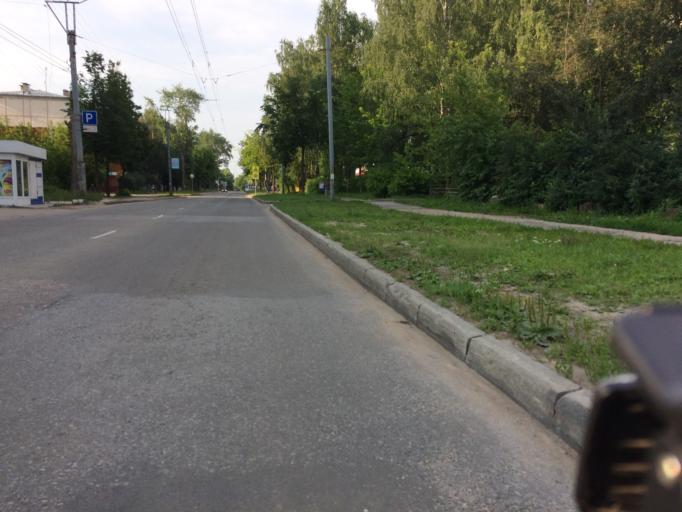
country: RU
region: Mariy-El
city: Yoshkar-Ola
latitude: 56.6226
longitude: 47.9457
